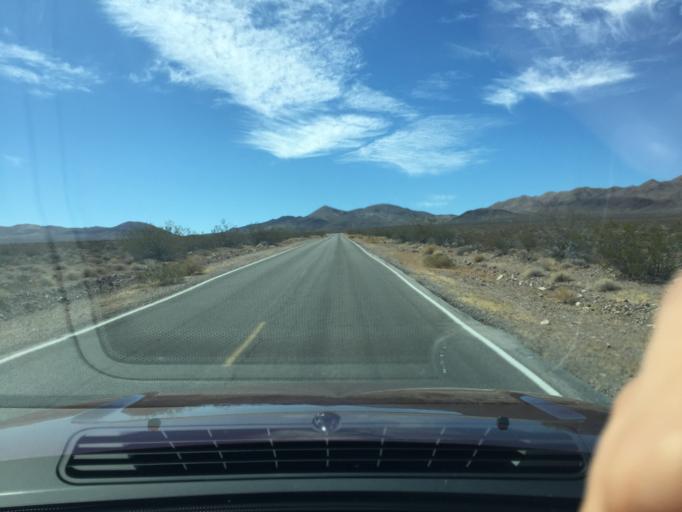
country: US
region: Nevada
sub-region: Nye County
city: Beatty
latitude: 36.2594
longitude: -116.6698
